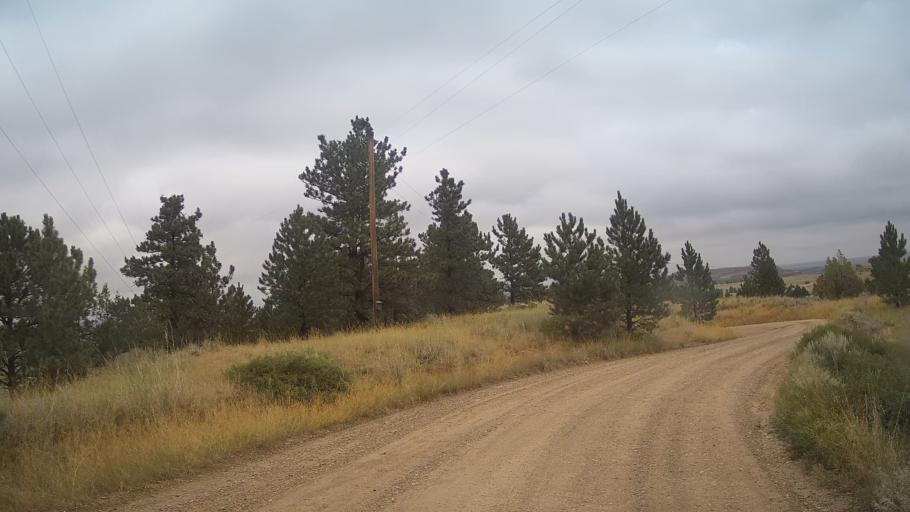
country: US
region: Montana
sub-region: Dawson County
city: Glendive
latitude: 47.0518
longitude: -104.6780
